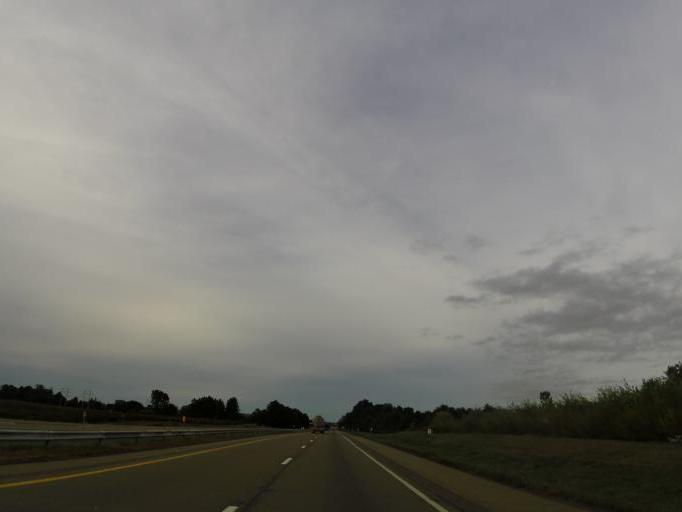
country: US
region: New York
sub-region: Chautauqua County
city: Silver Creek
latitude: 42.5275
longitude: -79.1373
